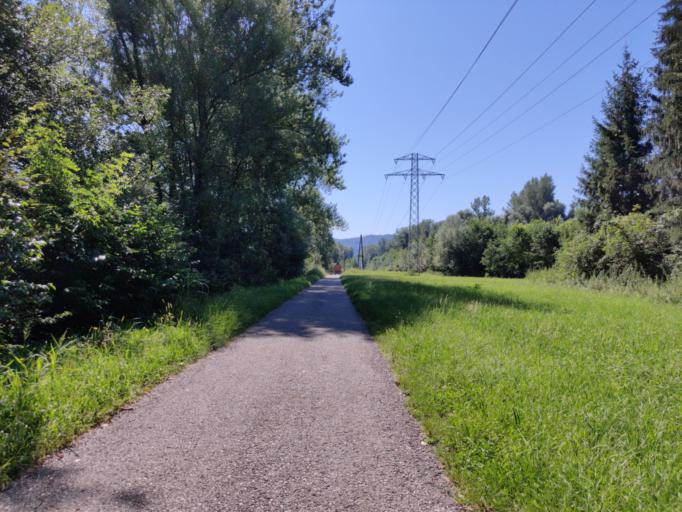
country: AT
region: Styria
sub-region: Politischer Bezirk Graz-Umgebung
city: Werndorf
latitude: 46.9040
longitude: 15.4910
